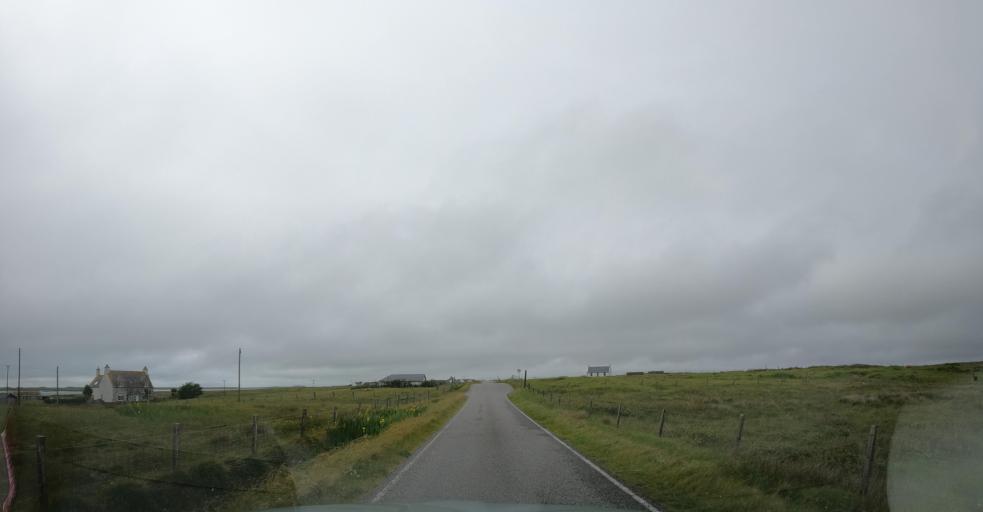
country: GB
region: Scotland
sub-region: Eilean Siar
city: Isle of North Uist
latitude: 57.5669
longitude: -7.3871
